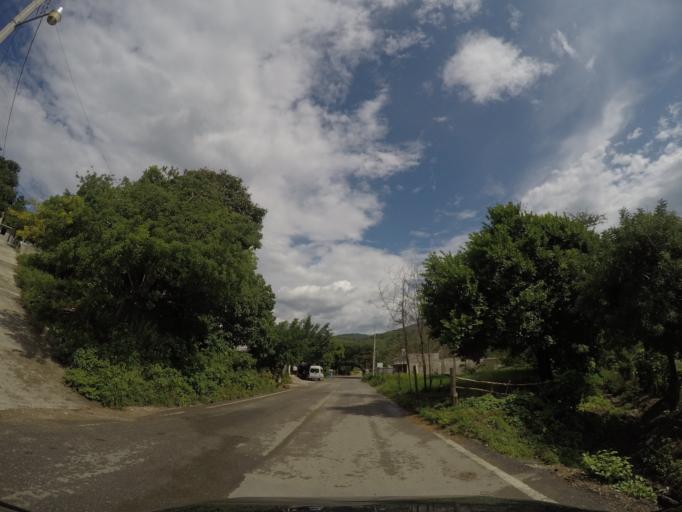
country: MX
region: Oaxaca
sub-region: San Jeronimo Coatlan
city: San Cristobal Honduras
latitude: 16.3530
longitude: -97.0958
